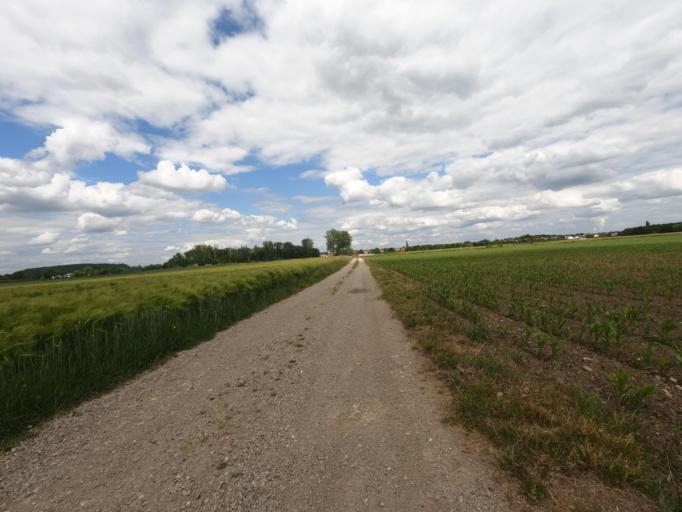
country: DE
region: North Rhine-Westphalia
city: Huckelhoven
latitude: 51.0302
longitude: 6.2018
